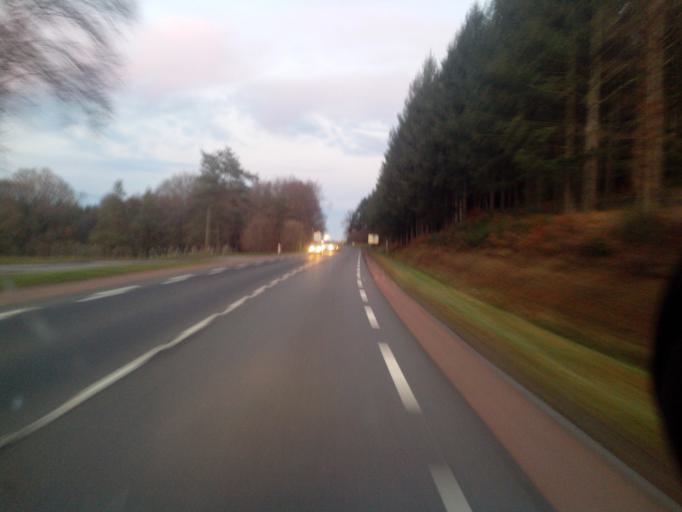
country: FR
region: Limousin
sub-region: Departement de la Correze
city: Ussel
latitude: 45.5100
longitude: 2.2484
